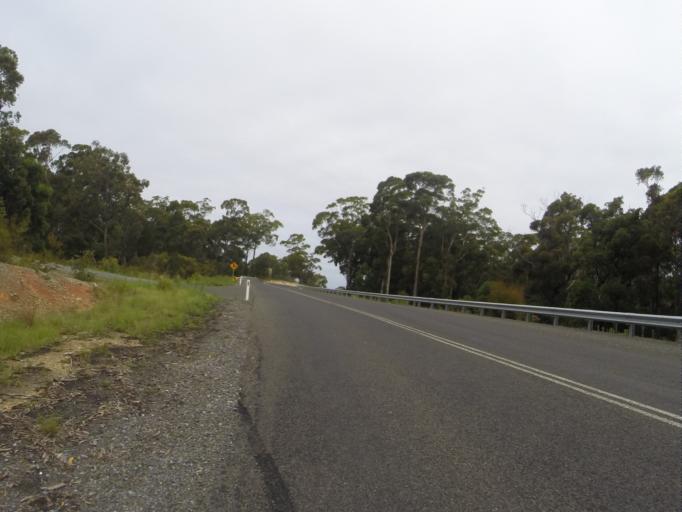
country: AU
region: New South Wales
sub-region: Eurobodalla
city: Broulee
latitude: -35.7816
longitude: 150.2172
